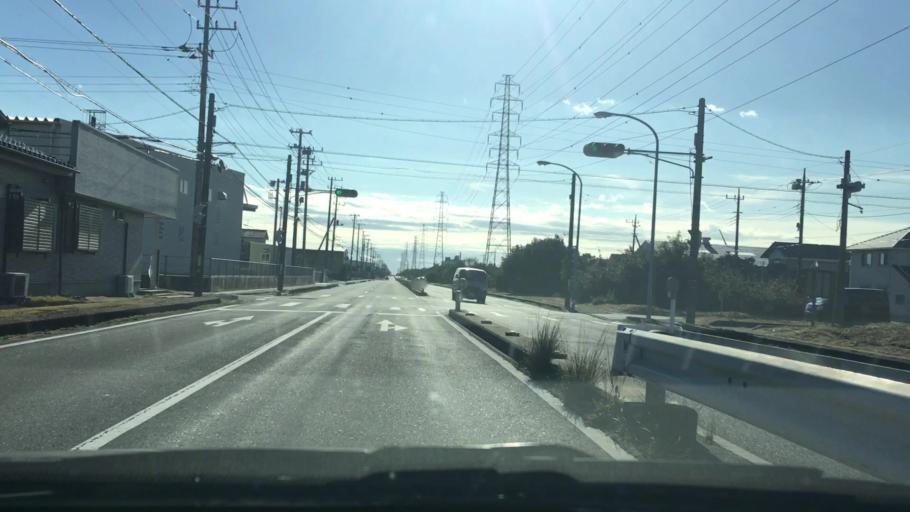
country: JP
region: Chiba
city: Omigawa
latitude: 35.8706
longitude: 140.7229
